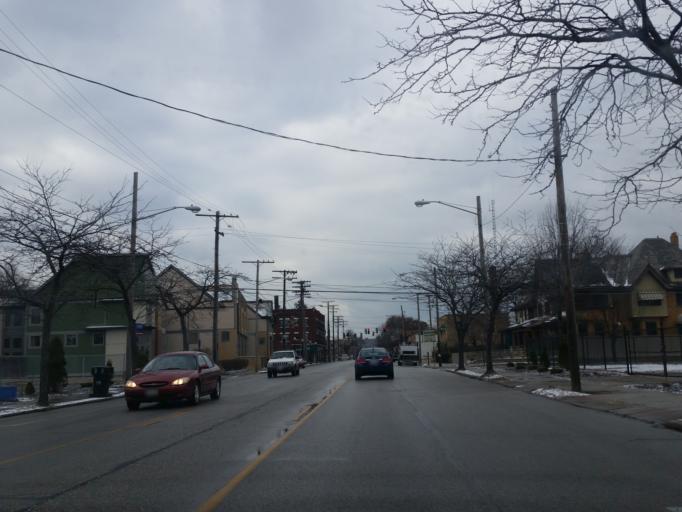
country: US
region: Ohio
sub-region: Cuyahoga County
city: Lakewood
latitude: 41.4841
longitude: -81.7734
